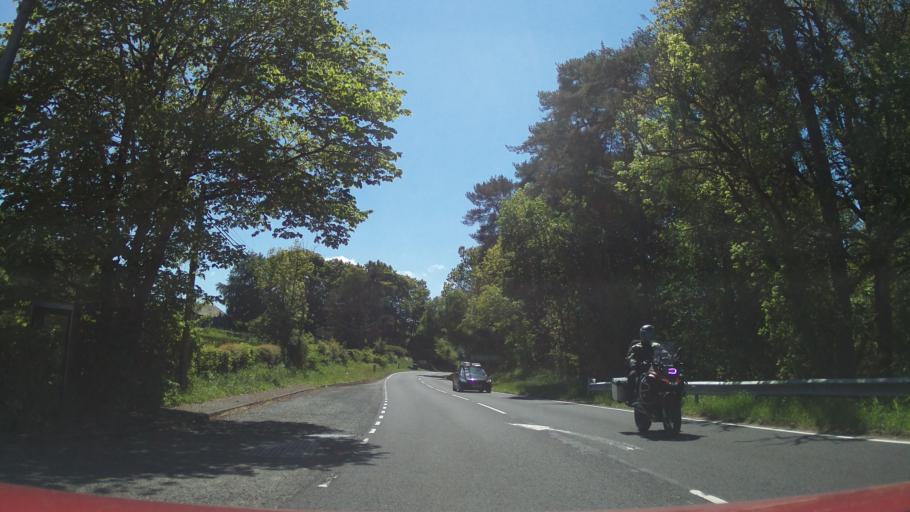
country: GB
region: Scotland
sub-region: The Scottish Borders
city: Hawick
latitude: 55.3626
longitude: -2.8913
